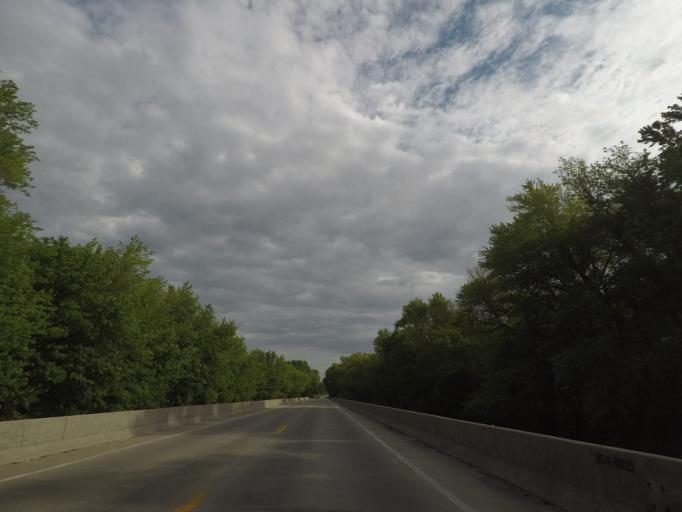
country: US
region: Illinois
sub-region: Logan County
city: Mount Pulaski
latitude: 40.0527
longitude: -89.2820
